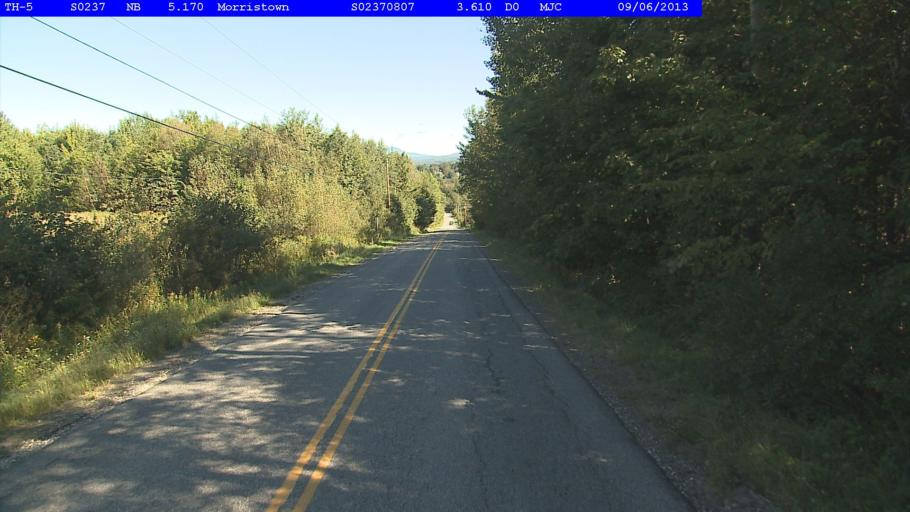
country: US
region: Vermont
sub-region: Lamoille County
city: Morristown
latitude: 44.5489
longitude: -72.6280
